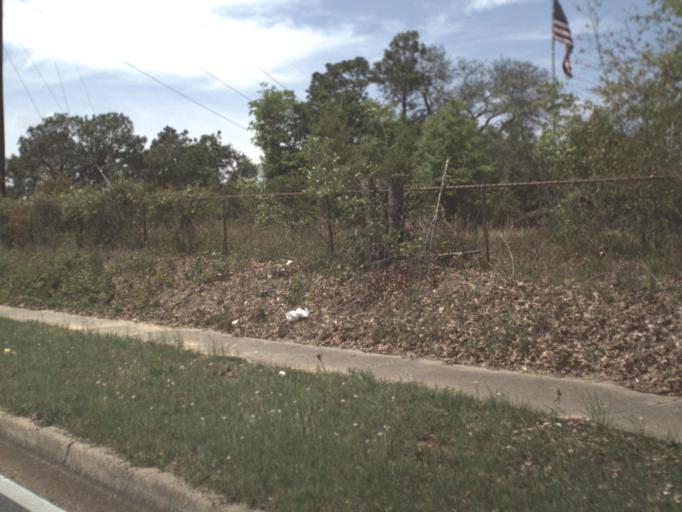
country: US
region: Florida
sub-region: Escambia County
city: Bellview
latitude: 30.4608
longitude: -87.2852
